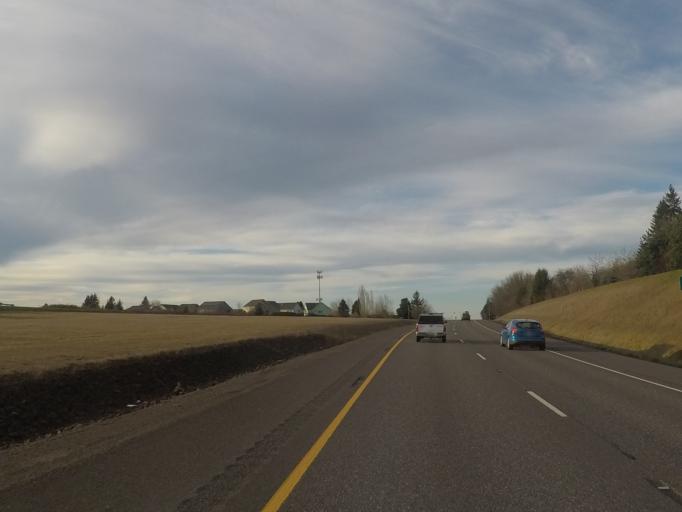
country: US
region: Oregon
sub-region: Multnomah County
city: Gresham
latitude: 45.4736
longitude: -122.3958
